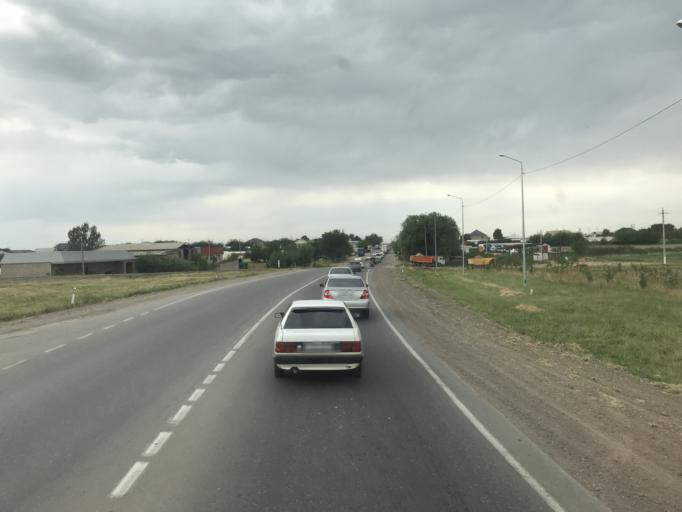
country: KZ
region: Ongtustik Qazaqstan
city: Saryaghash
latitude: 41.4328
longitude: 69.1124
